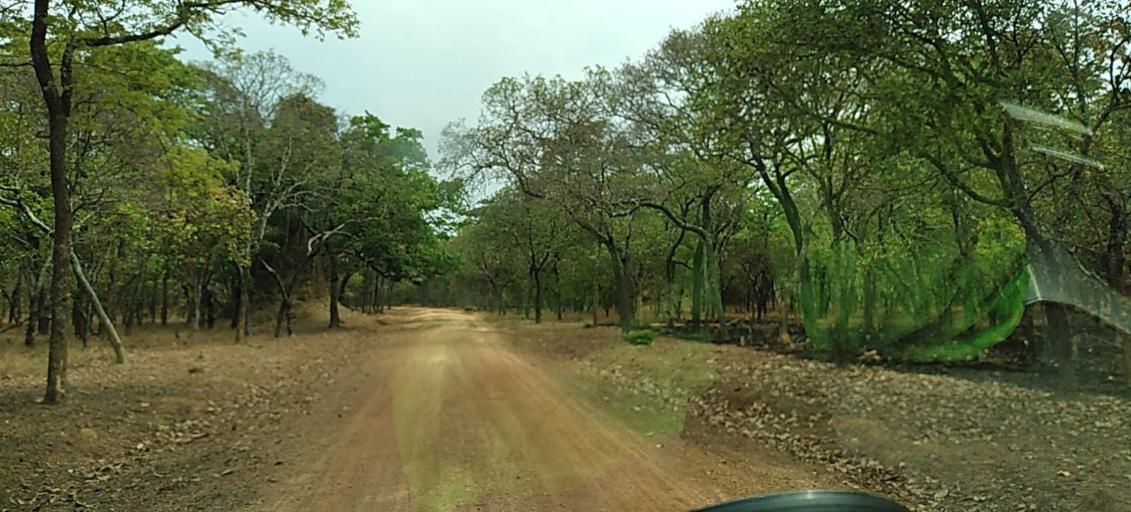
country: ZM
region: North-Western
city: Solwezi
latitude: -12.9395
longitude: 26.5582
